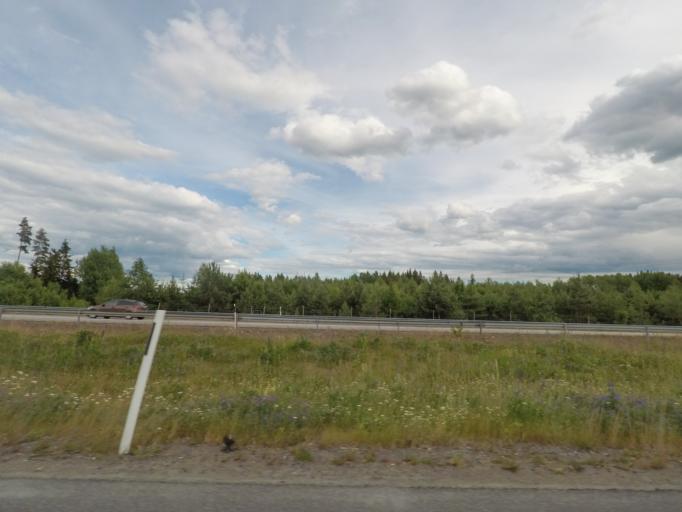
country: FI
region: Uusimaa
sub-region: Helsinki
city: Maentsaelae
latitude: 60.6618
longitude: 25.3289
